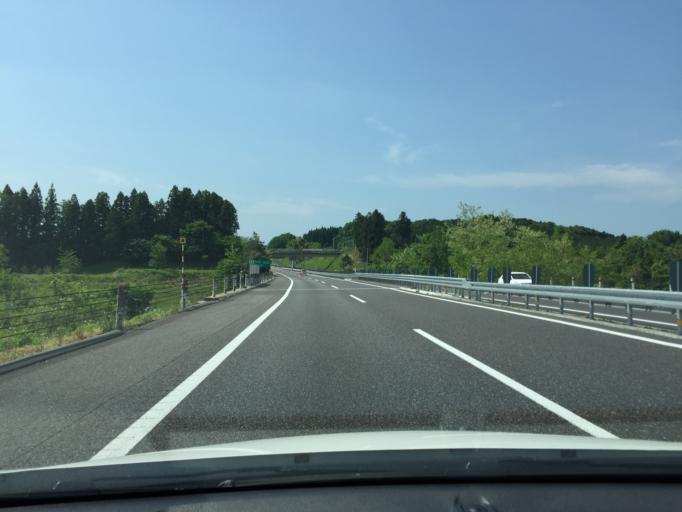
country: JP
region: Fukushima
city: Sukagawa
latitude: 37.2145
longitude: 140.3089
